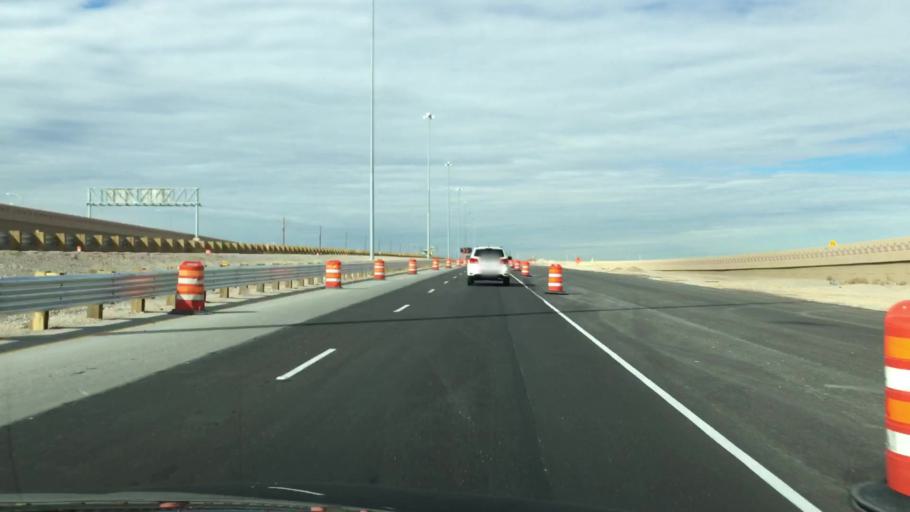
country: US
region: Nevada
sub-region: Clark County
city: Summerlin South
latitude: 36.3152
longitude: -115.3011
